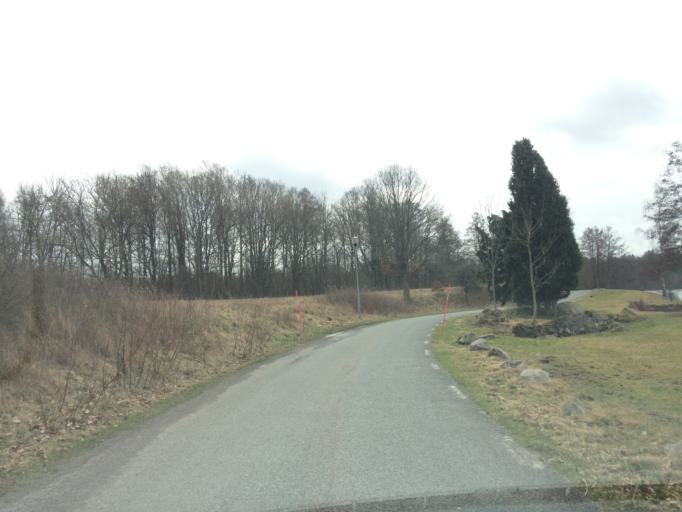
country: SE
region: Skane
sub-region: Ostra Goinge Kommun
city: Sibbhult
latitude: 56.2796
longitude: 14.3038
